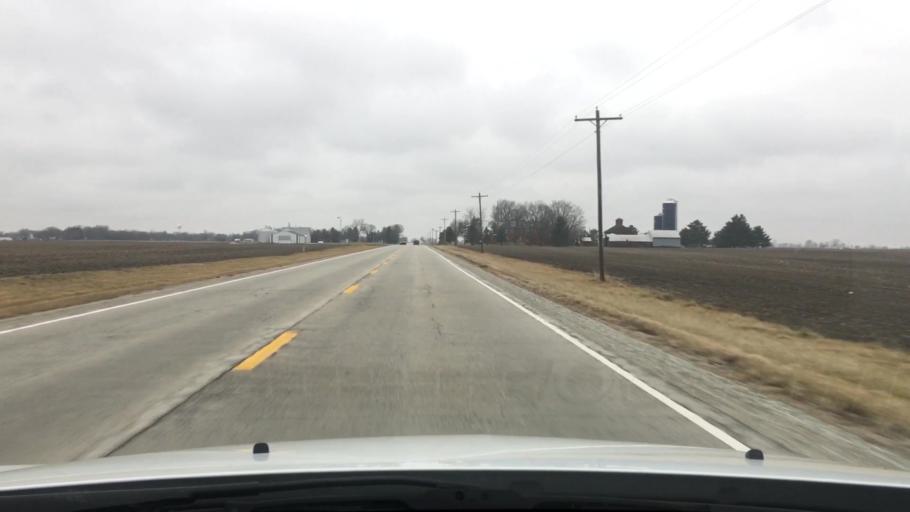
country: US
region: Illinois
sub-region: Iroquois County
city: Clifton
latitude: 40.8855
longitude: -87.9263
